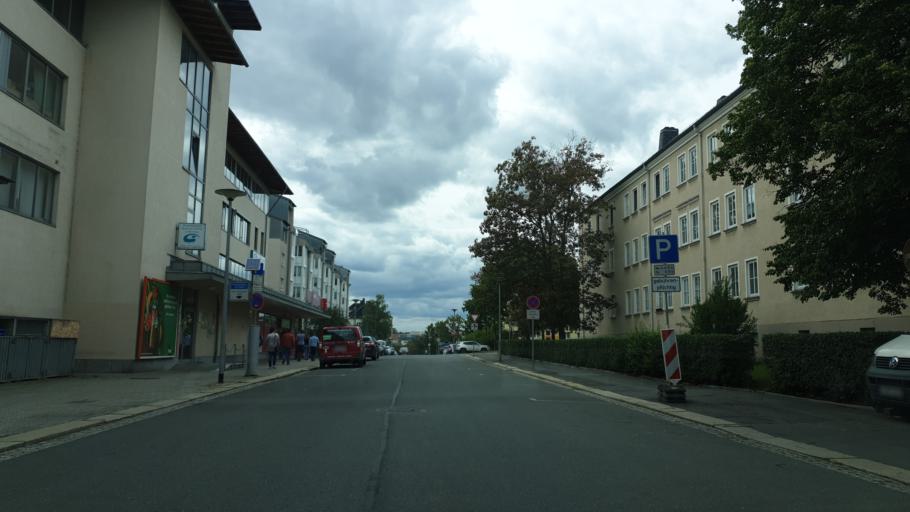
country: DE
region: Saxony
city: Plauen
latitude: 50.5012
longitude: 12.1353
